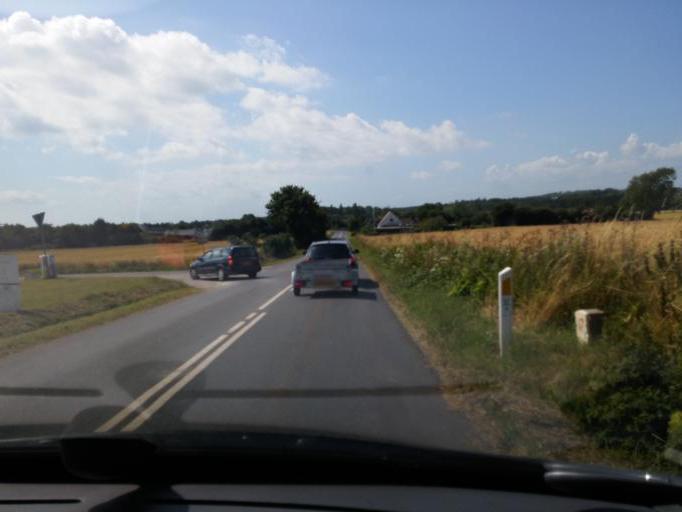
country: DK
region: South Denmark
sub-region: Langeland Kommune
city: Rudkobing
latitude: 54.8175
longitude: 10.6622
